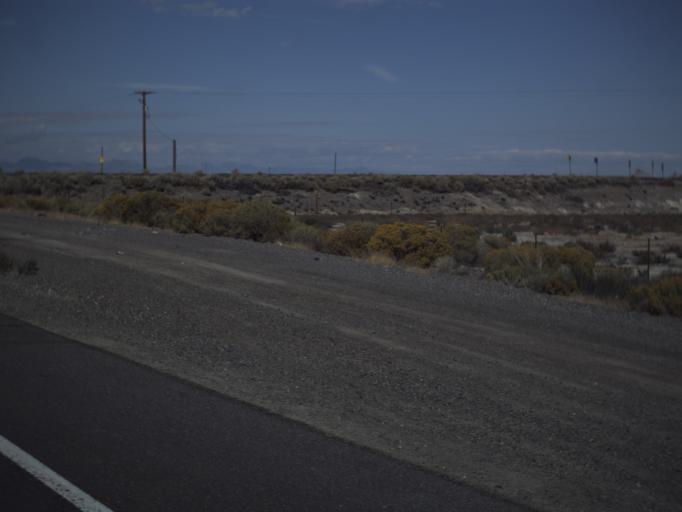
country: US
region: Utah
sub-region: Tooele County
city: Wendover
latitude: 40.7278
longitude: -113.2574
